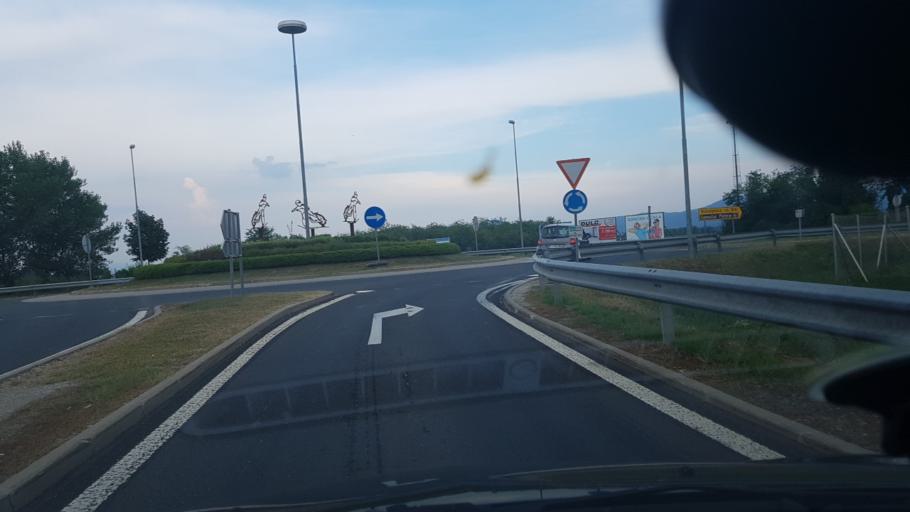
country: SI
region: Krsko
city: Leskovec pri Krskem
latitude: 45.9155
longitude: 15.4704
